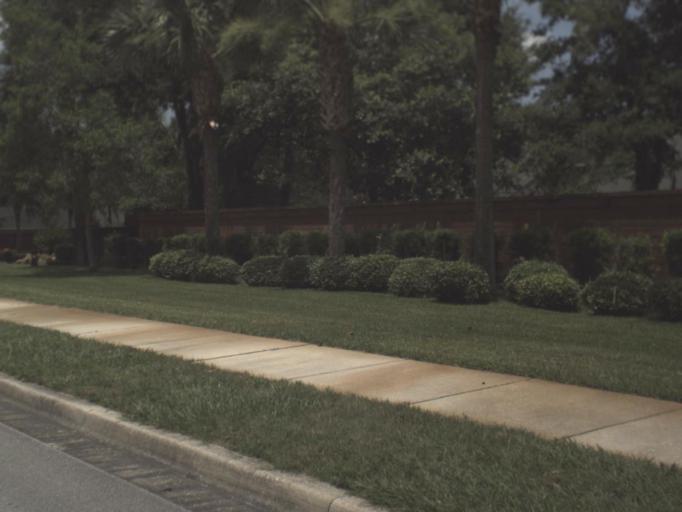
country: US
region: Florida
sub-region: Alachua County
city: Alachua
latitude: 29.6564
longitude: -82.4827
